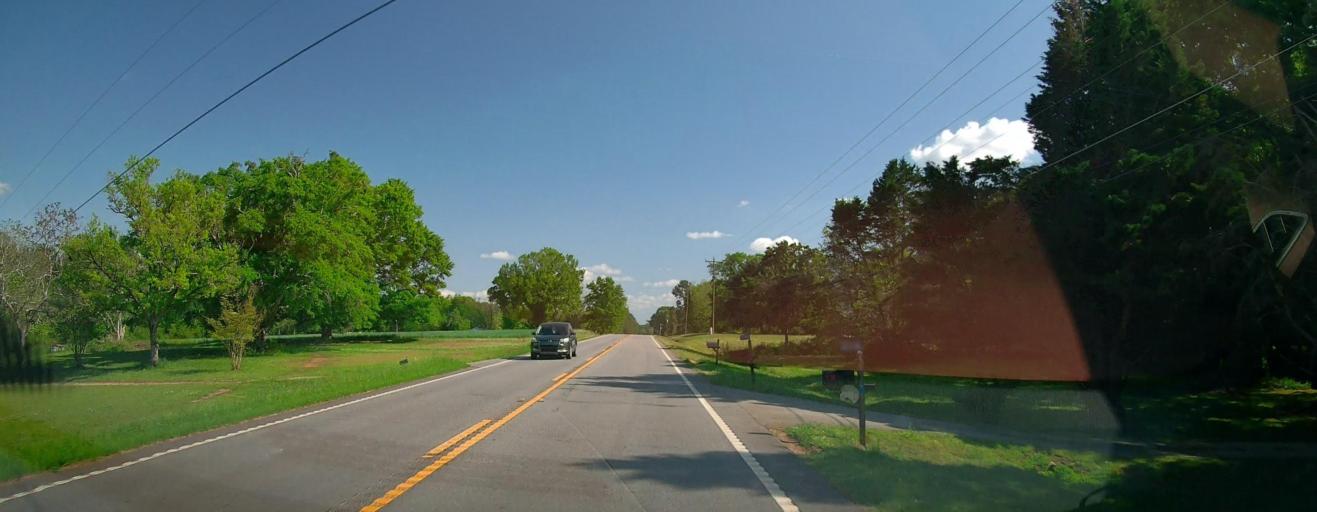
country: US
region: Georgia
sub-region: Morgan County
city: Madison
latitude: 33.6261
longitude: -83.4846
